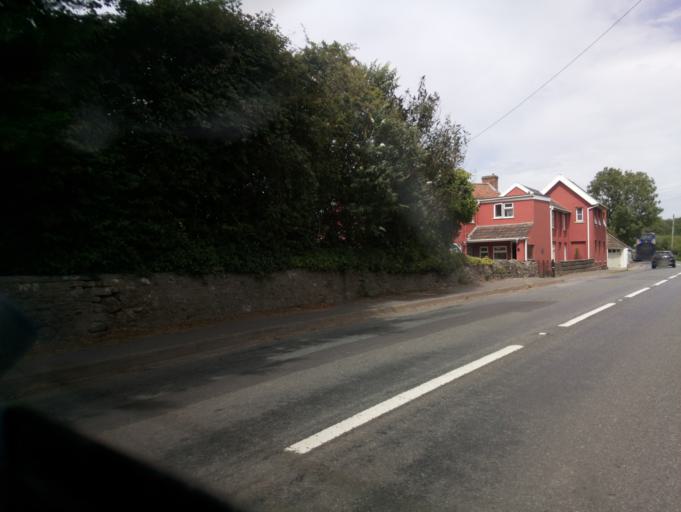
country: GB
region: England
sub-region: Somerset
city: Wells
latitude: 51.1934
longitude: -2.6698
